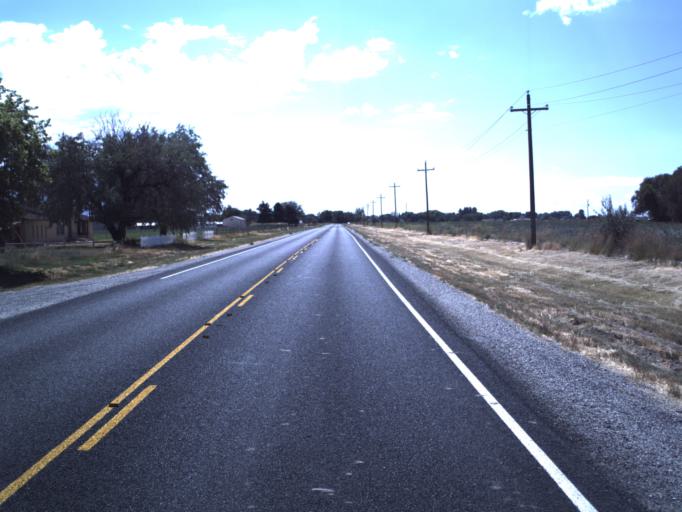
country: US
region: Utah
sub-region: Box Elder County
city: Honeyville
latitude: 41.6356
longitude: -112.1284
